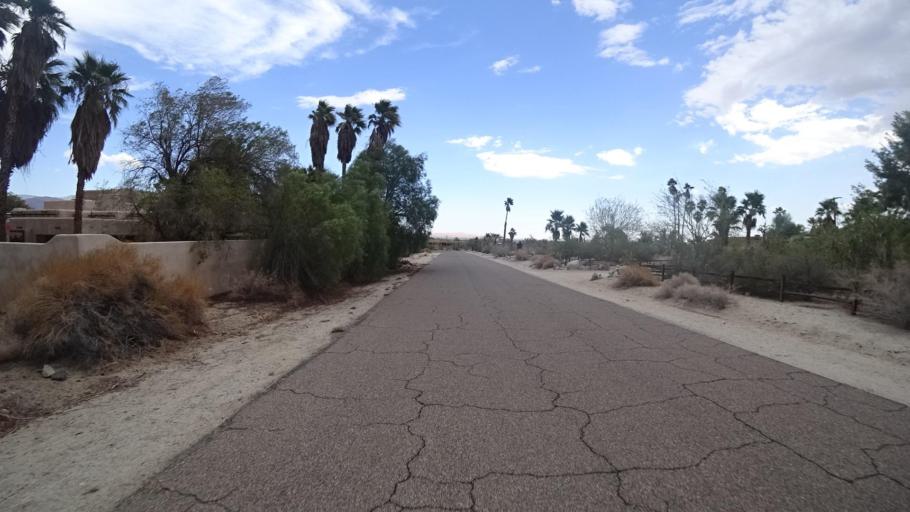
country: US
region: California
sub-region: San Diego County
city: Borrego Springs
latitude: 33.2608
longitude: -116.3966
